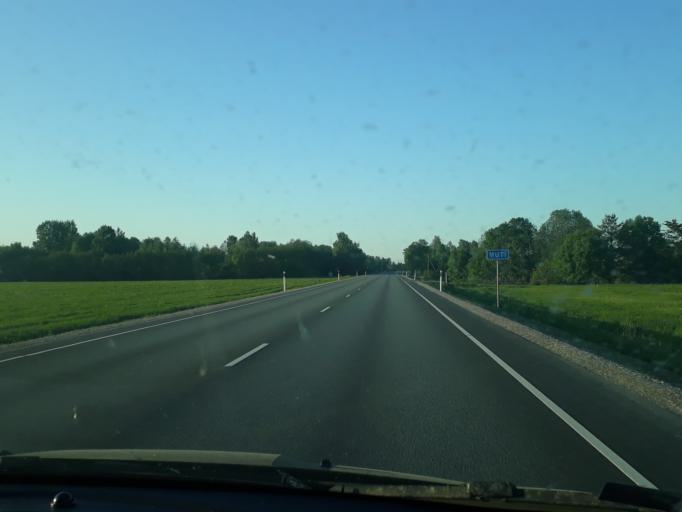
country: EE
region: Paernumaa
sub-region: Tootsi vald
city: Tootsi
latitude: 58.5316
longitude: 24.8312
